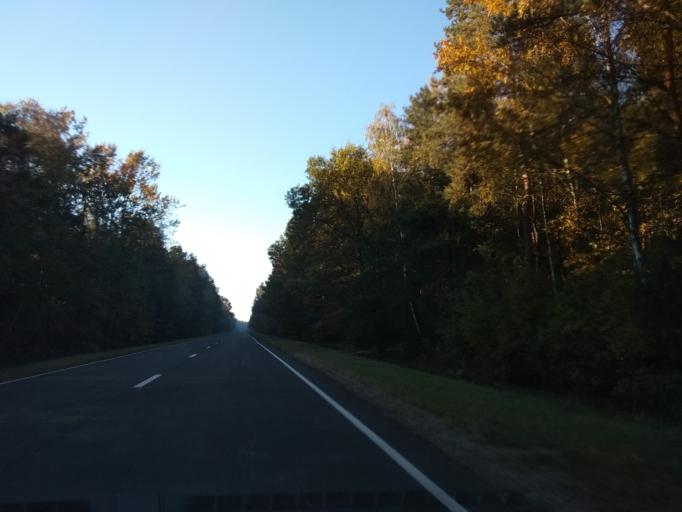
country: BY
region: Brest
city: Kobryn
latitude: 52.0451
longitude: 24.2752
